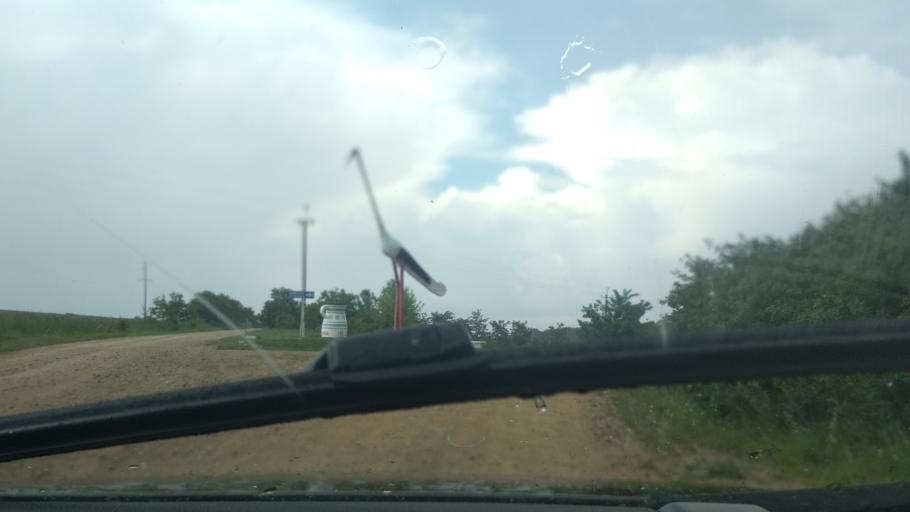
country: MD
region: Singerei
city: Biruinta
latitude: 47.7411
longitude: 28.1366
